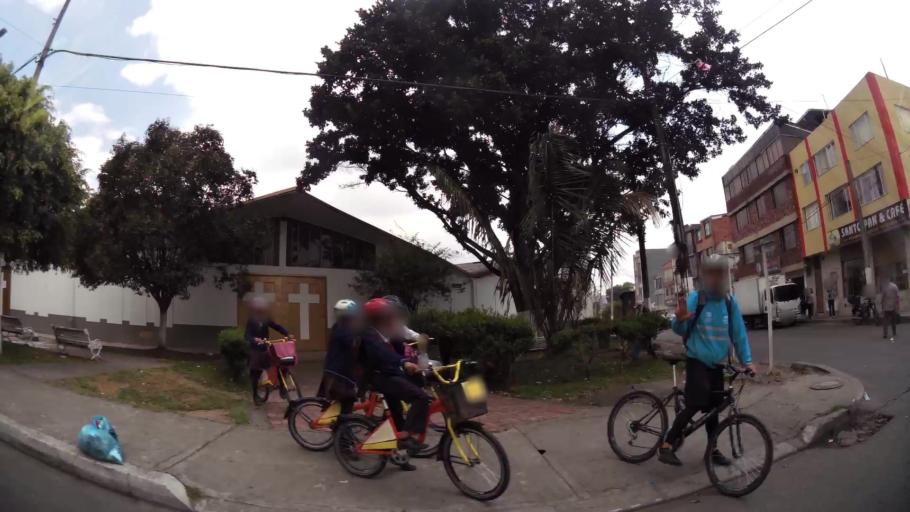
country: CO
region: Cundinamarca
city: La Calera
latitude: 4.7372
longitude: -74.0281
